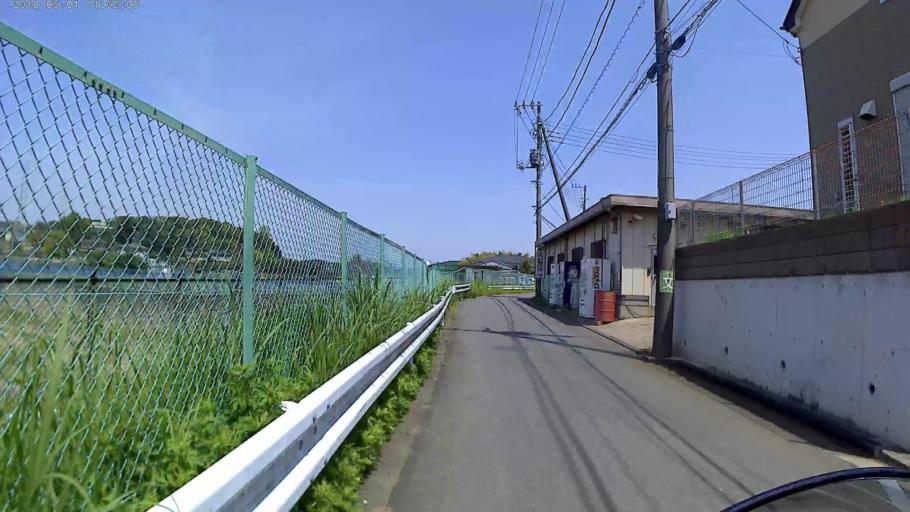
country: JP
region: Kanagawa
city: Minami-rinkan
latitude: 35.4809
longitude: 139.5189
